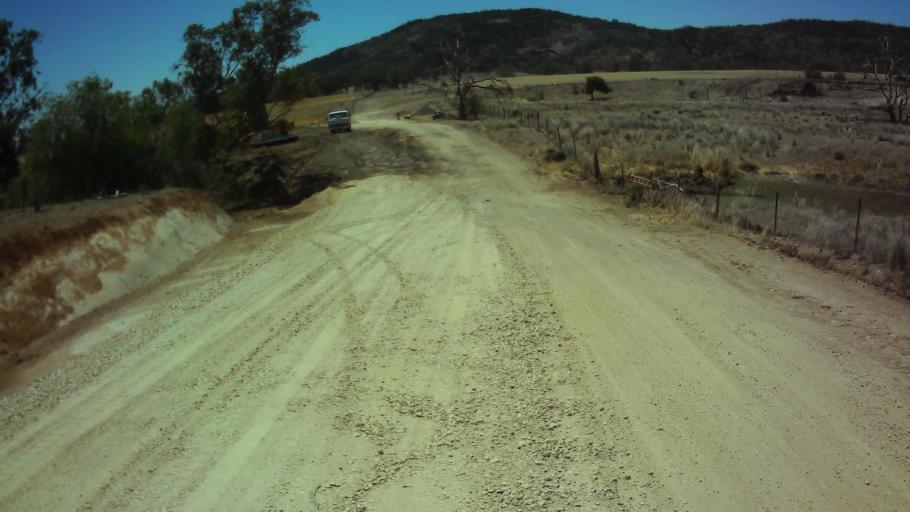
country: AU
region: New South Wales
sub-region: Weddin
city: Grenfell
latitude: -33.8547
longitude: 148.1080
